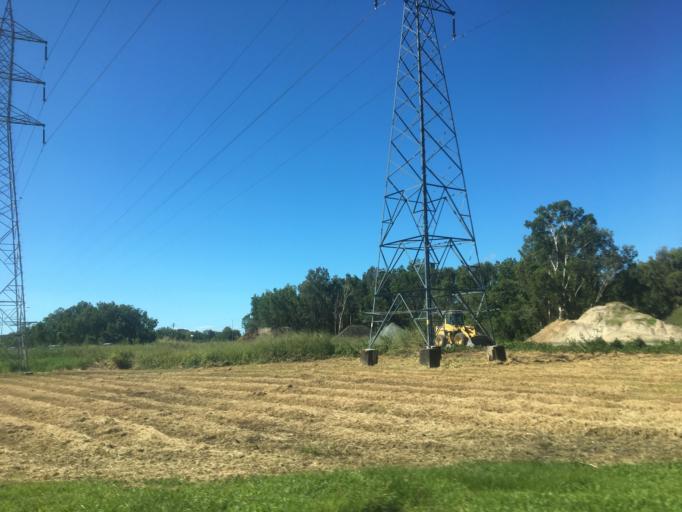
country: AU
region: Queensland
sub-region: Cairns
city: Woree
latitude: -16.9524
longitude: 145.7523
